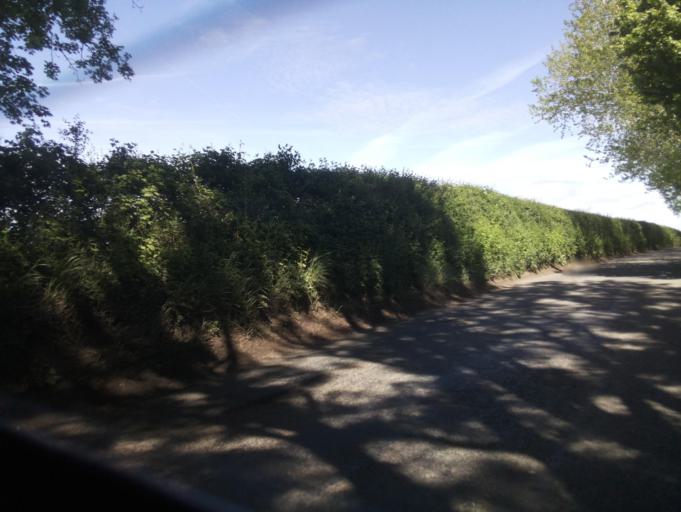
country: GB
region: England
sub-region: Devon
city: Ottery St Mary
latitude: 50.7677
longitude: -3.2642
